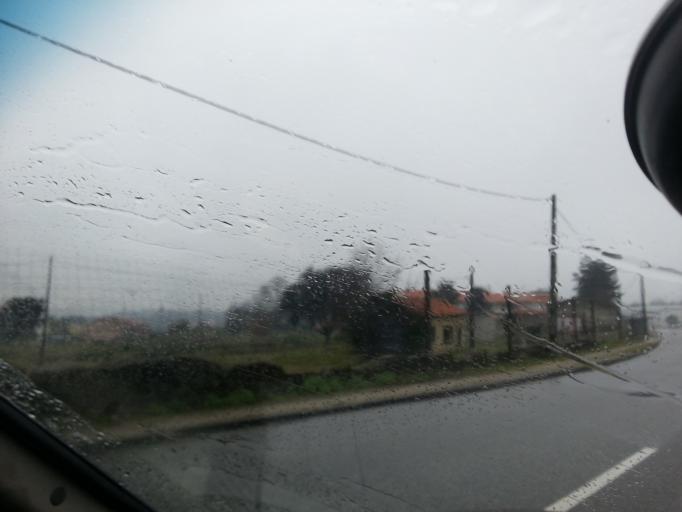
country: PT
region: Viseu
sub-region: Mangualde
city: Mangualde
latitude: 40.6049
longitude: -7.7735
